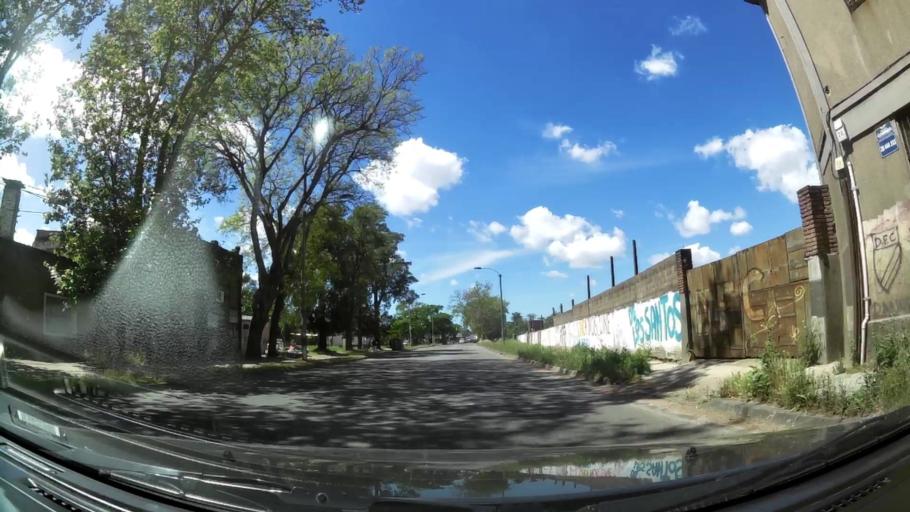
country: UY
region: Montevideo
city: Montevideo
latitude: -34.8435
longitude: -56.1361
